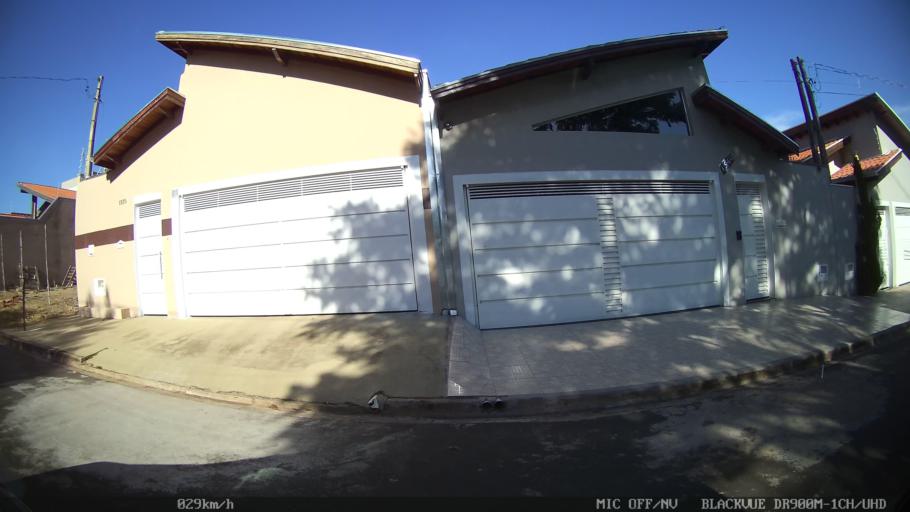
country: BR
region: Sao Paulo
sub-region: Franca
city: Franca
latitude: -20.5128
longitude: -47.4283
